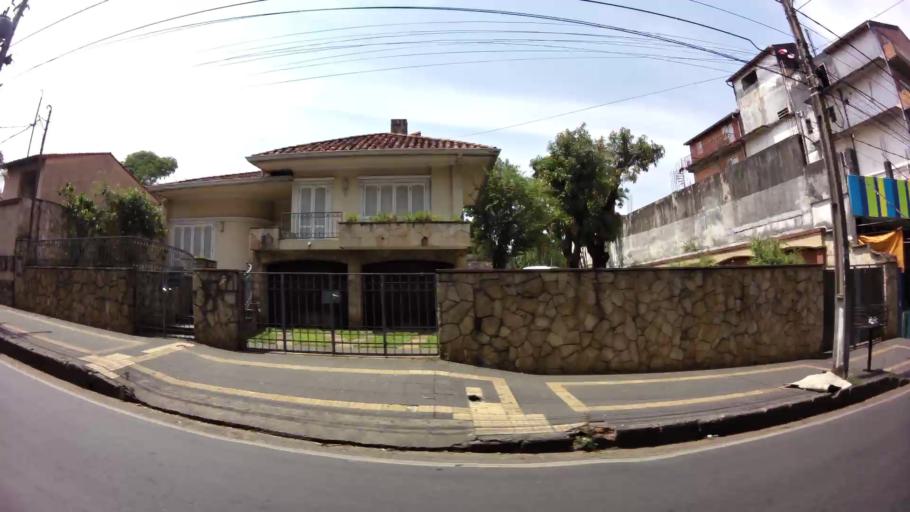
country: PY
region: Central
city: Lambare
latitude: -25.3213
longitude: -57.5939
